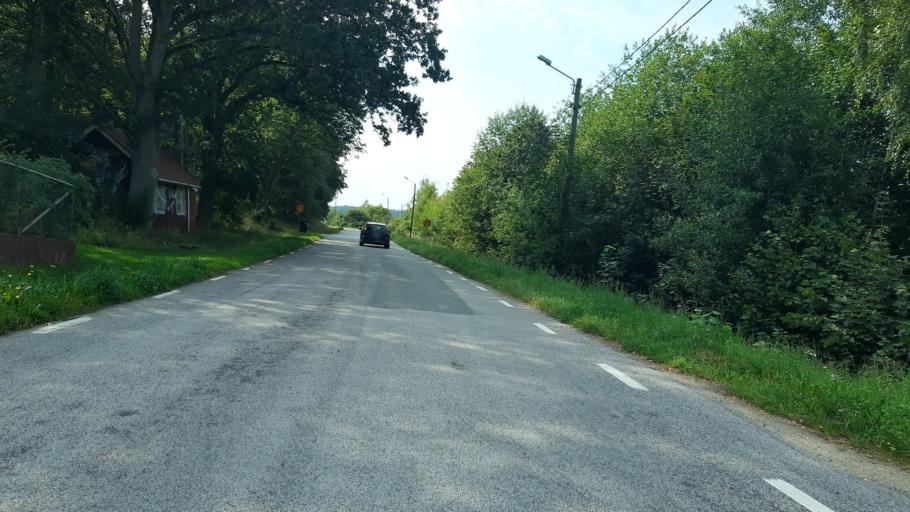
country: SE
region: Blekinge
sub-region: Ronneby Kommun
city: Kallinge
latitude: 56.2170
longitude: 15.3585
